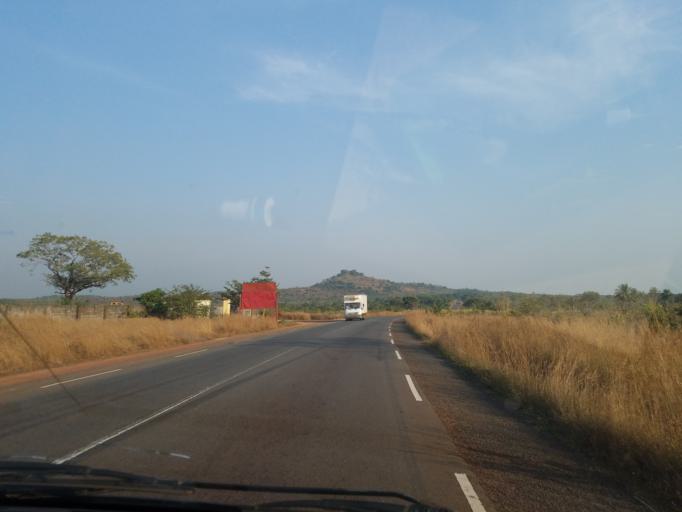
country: GN
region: Boke
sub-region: Boffa
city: Boffa
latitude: 10.3509
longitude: -14.2514
